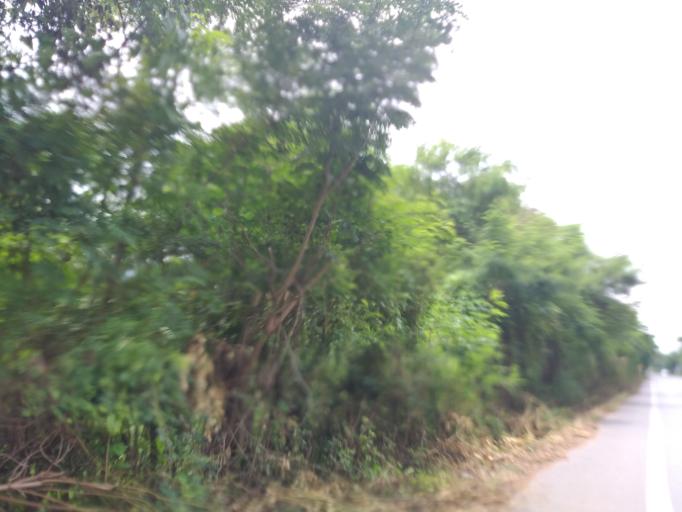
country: TH
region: Pathum Thani
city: Nong Suea
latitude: 14.0652
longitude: 100.8717
